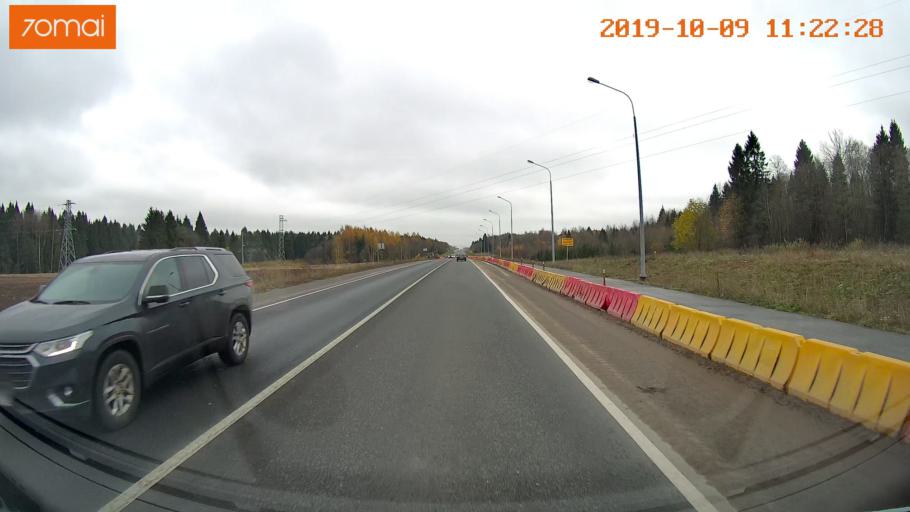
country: RU
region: Vologda
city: Vologda
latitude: 59.1315
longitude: 39.9582
